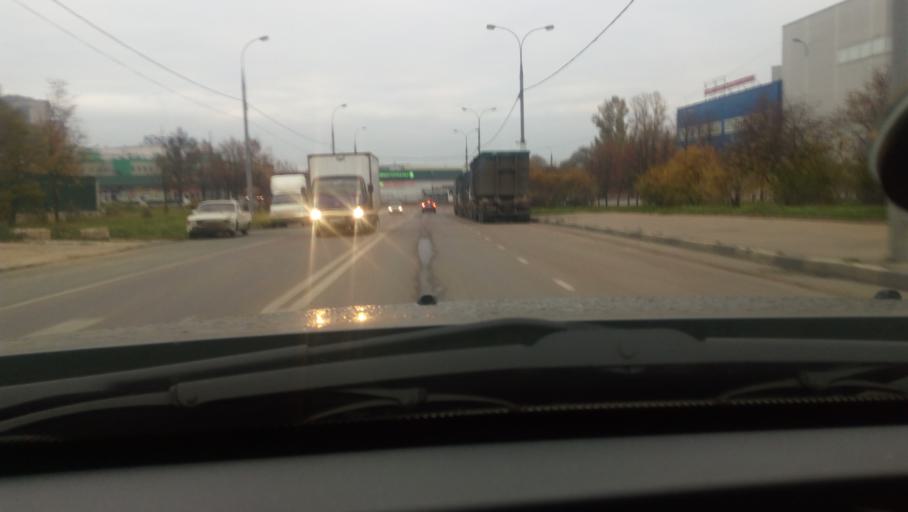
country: RU
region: Moskovskaya
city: Reutov
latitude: 55.7474
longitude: 37.8858
